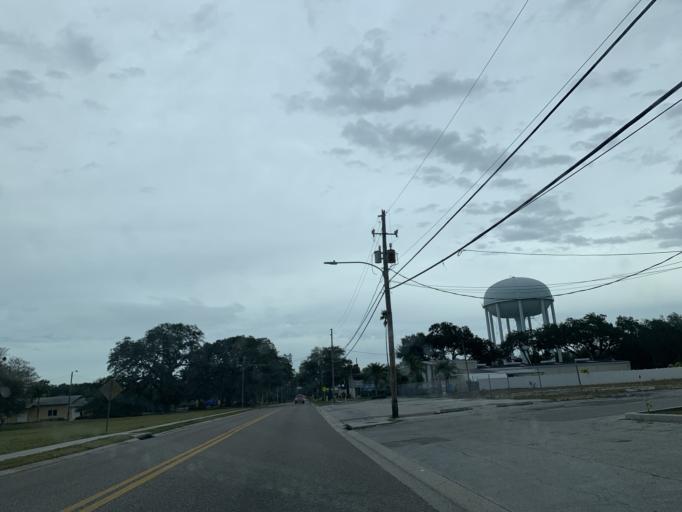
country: US
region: Florida
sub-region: Pinellas County
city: Belleair
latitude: 27.9433
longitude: -82.7916
